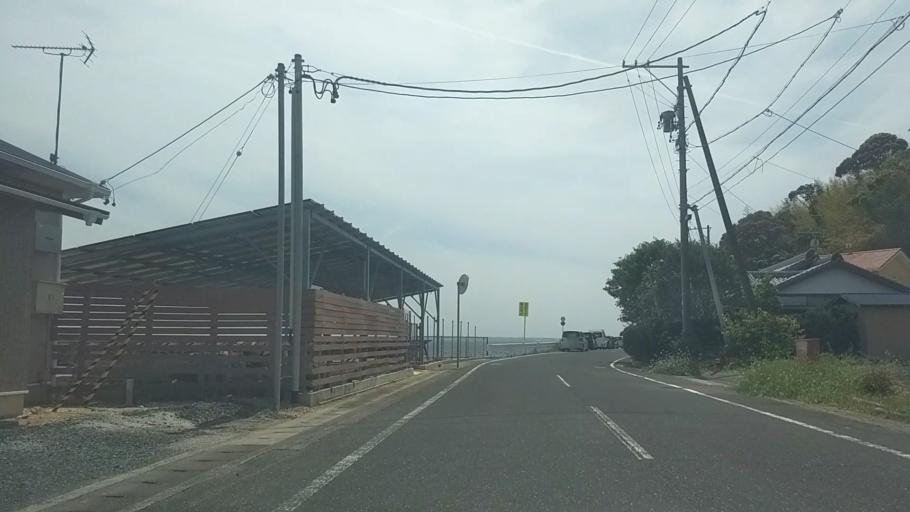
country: JP
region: Shizuoka
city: Kosai-shi
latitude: 34.7854
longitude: 137.5956
